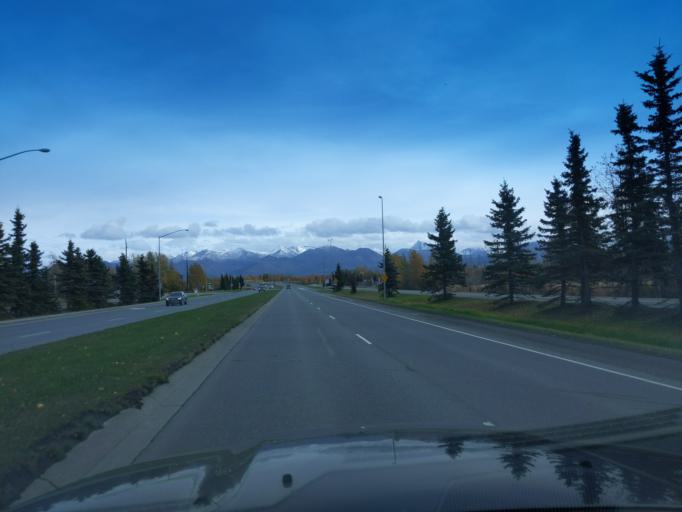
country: US
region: Alaska
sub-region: Anchorage Municipality
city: Anchorage
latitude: 61.1730
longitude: -149.9313
